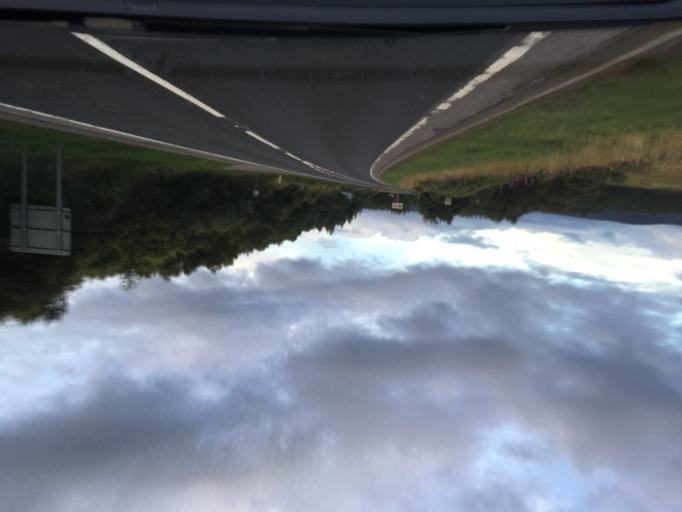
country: GB
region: Scotland
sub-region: Highland
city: Inverness
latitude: 57.3633
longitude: -4.0158
